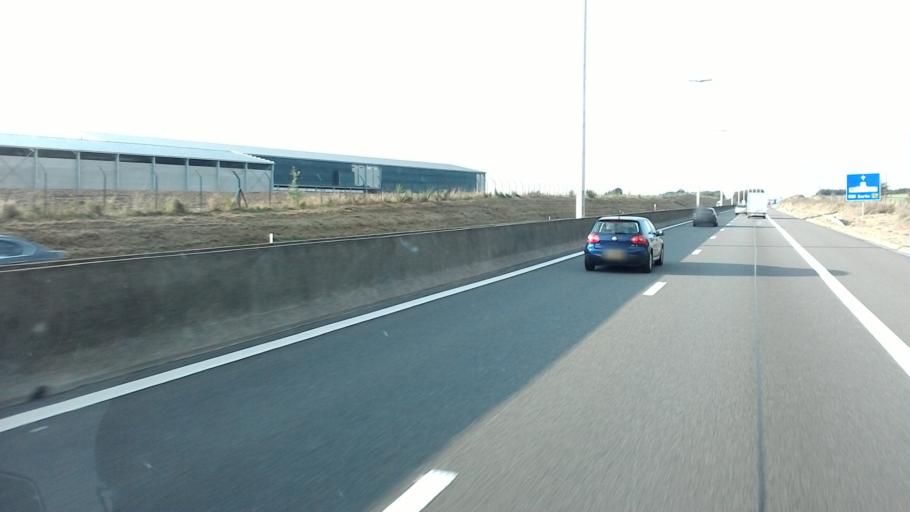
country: BE
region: Wallonia
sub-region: Province du Luxembourg
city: Leglise
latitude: 49.8352
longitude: 5.5120
